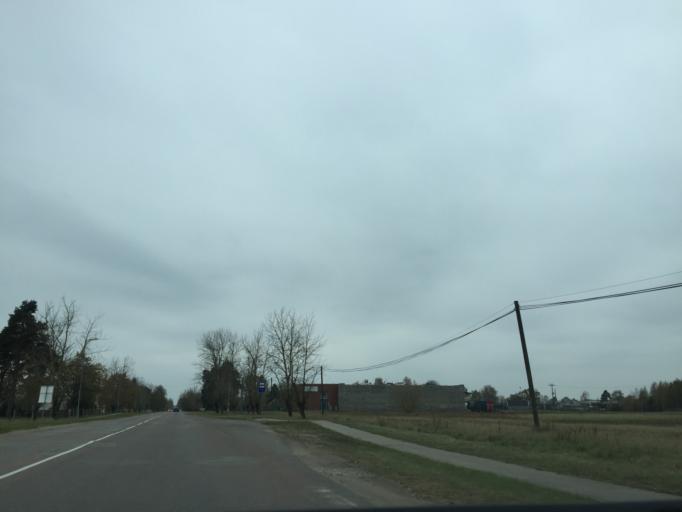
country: LV
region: Marupe
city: Marupe
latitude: 56.8875
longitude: 24.0713
